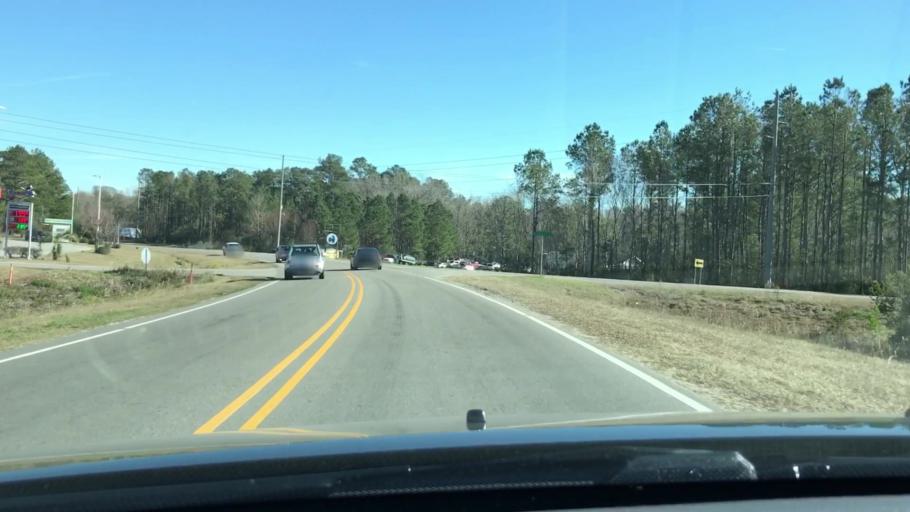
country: US
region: North Carolina
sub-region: Brunswick County
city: Shallotte
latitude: 33.9601
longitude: -78.4160
